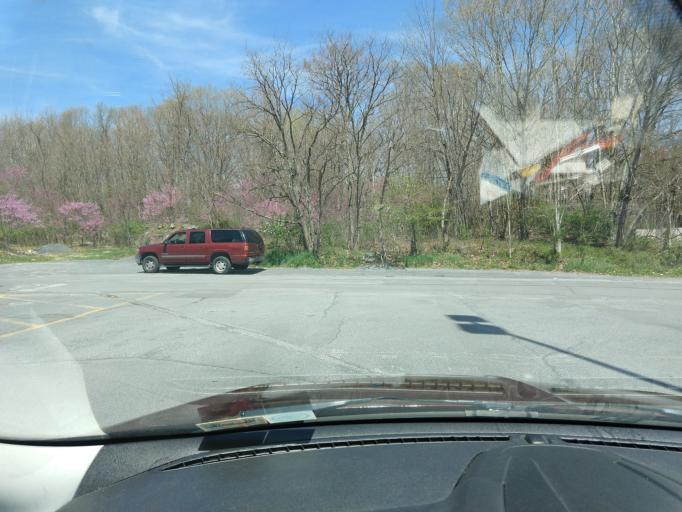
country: US
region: West Virginia
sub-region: Greenbrier County
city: Fairlea
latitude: 37.7896
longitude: -80.4514
